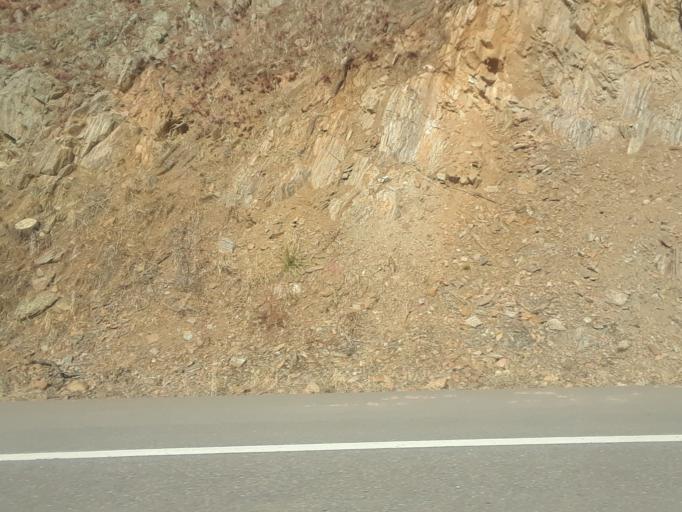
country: US
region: Colorado
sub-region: Boulder County
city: Boulder
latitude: 40.1085
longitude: -105.3343
